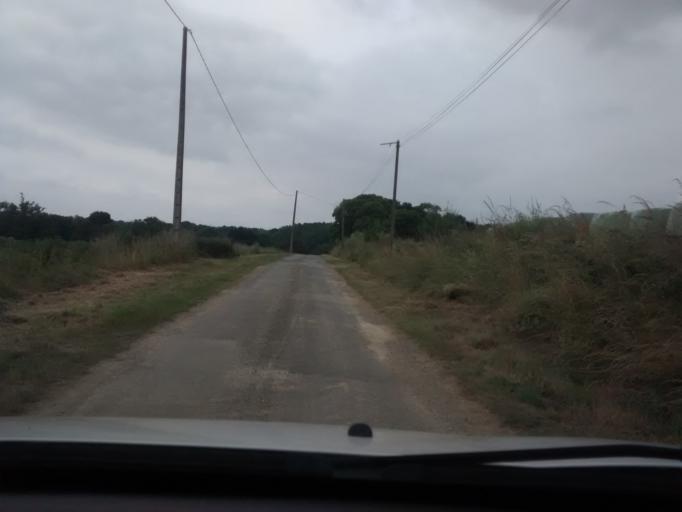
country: FR
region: Brittany
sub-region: Departement d'Ille-et-Vilaine
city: Noyal-sur-Vilaine
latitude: 48.1236
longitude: -1.5046
